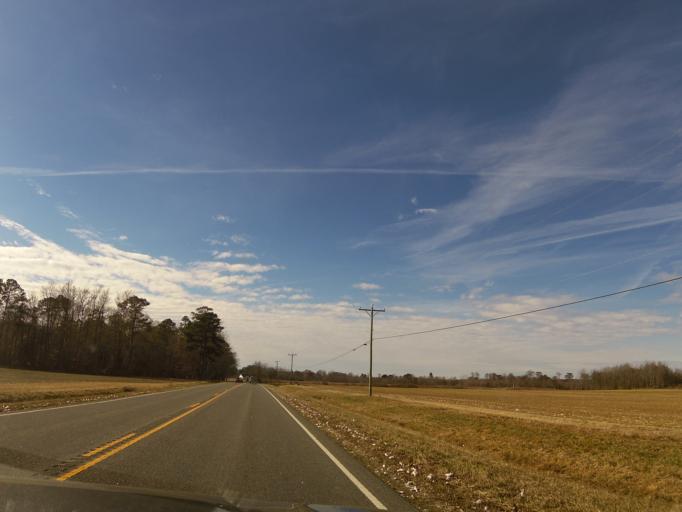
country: US
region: Virginia
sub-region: Isle of Wight County
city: Windsor
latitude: 36.7843
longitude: -76.8092
